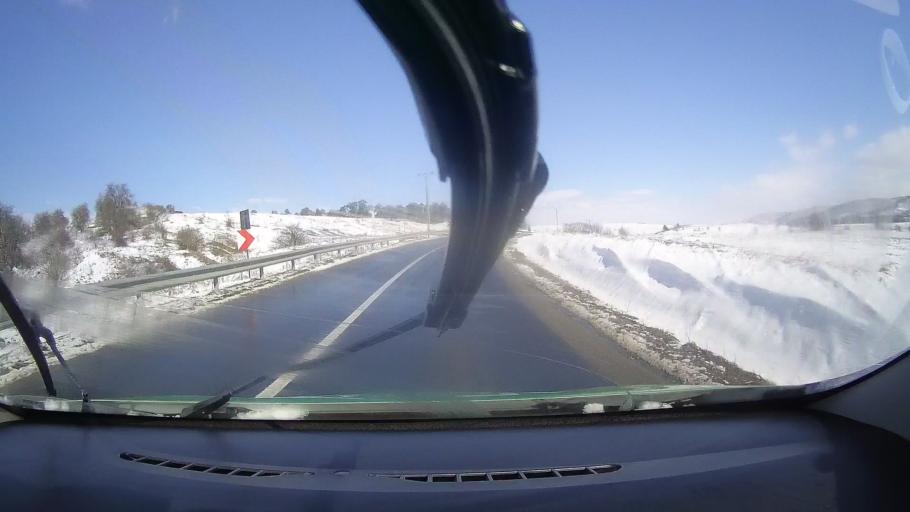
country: RO
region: Sibiu
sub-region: Comuna Rosia
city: Rosia
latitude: 45.8118
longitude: 24.3609
